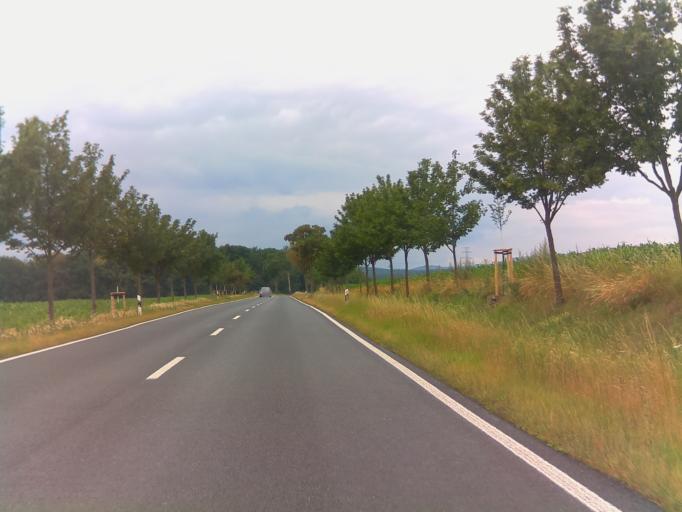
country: DE
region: Thuringia
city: Behringen
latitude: 50.7443
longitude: 11.0303
